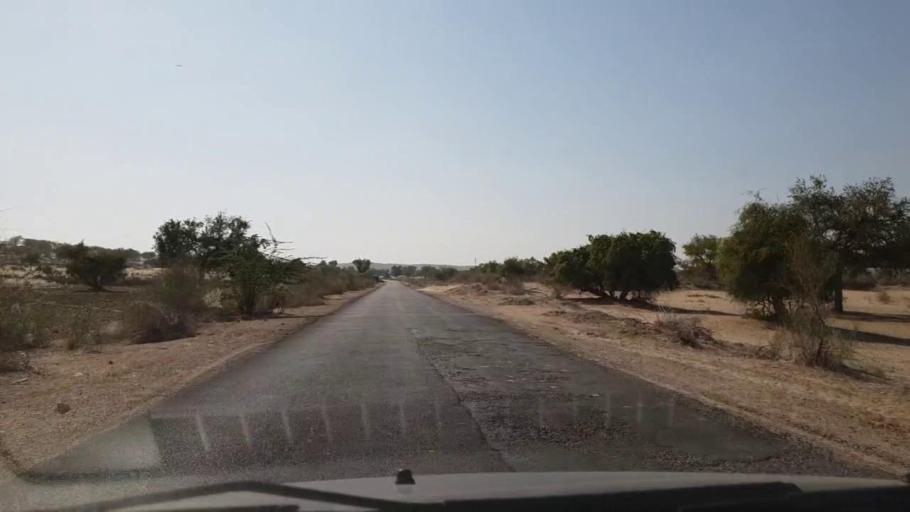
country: PK
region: Sindh
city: Mithi
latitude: 24.6631
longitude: 69.7593
